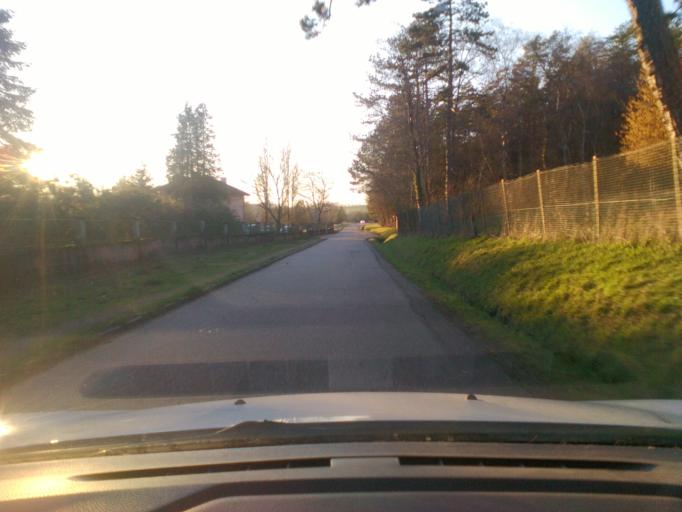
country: FR
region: Lorraine
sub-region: Departement des Vosges
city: Mirecourt
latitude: 48.2975
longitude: 6.1108
